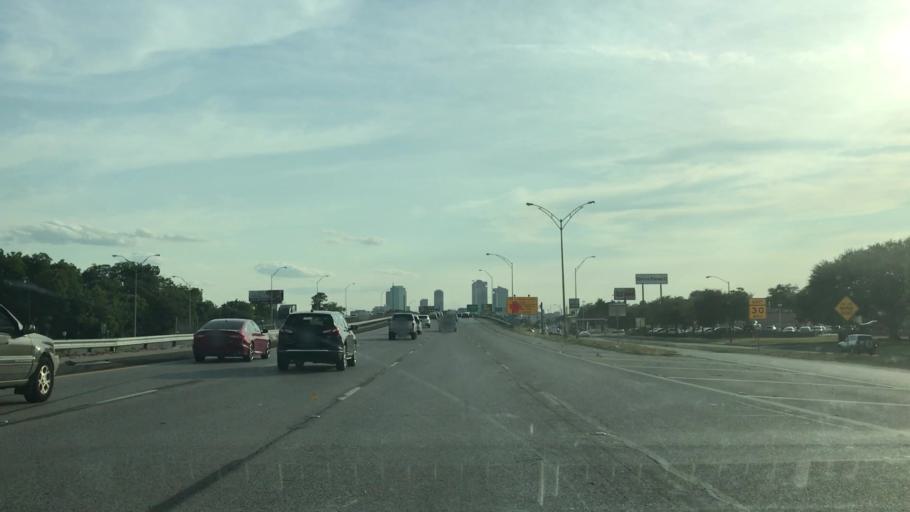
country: US
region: Texas
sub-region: Tarrant County
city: Haltom City
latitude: 32.7699
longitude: -97.2988
